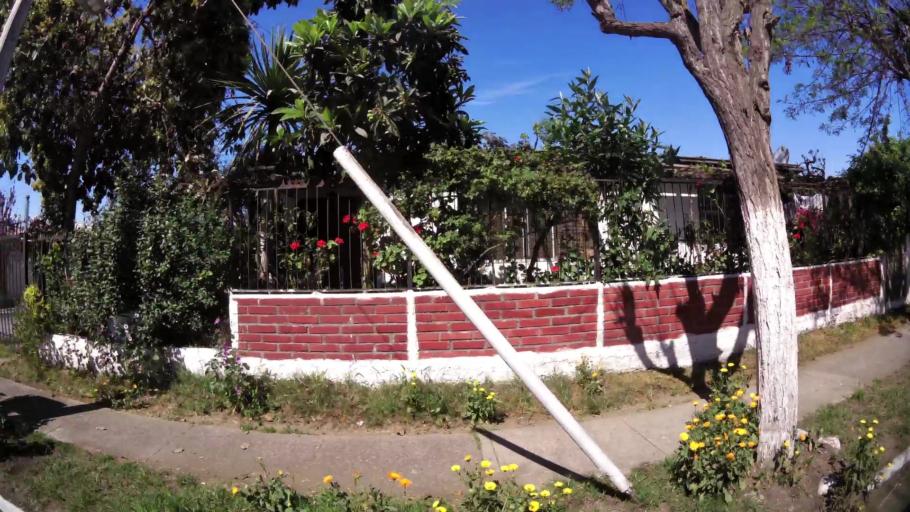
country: CL
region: Santiago Metropolitan
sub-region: Provincia de Talagante
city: Penaflor
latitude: -33.6009
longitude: -70.8827
